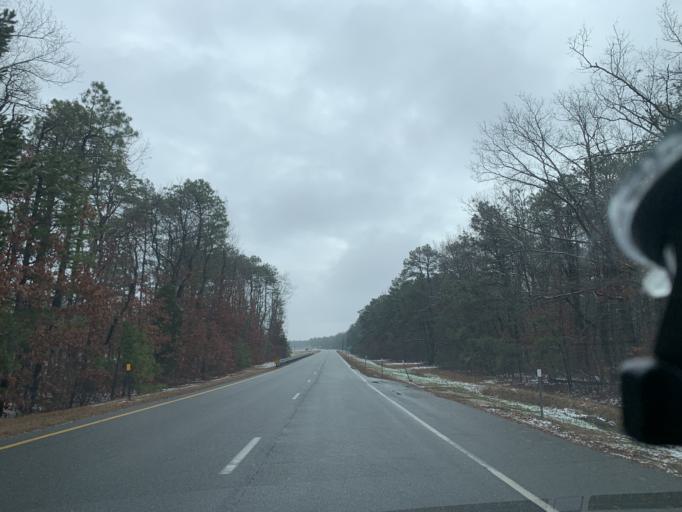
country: US
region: New Jersey
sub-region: Atlantic County
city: Pomona
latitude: 39.4484
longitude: -74.6238
